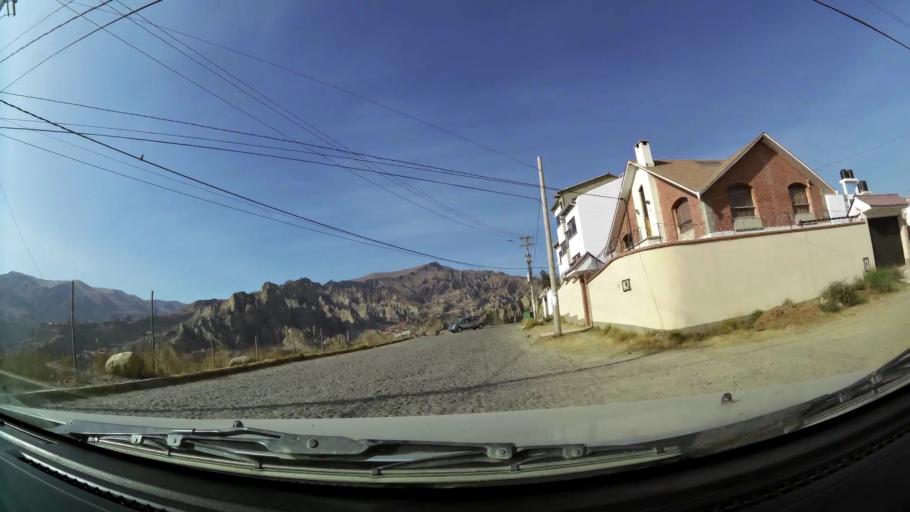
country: BO
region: La Paz
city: La Paz
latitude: -16.5079
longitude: -68.0824
